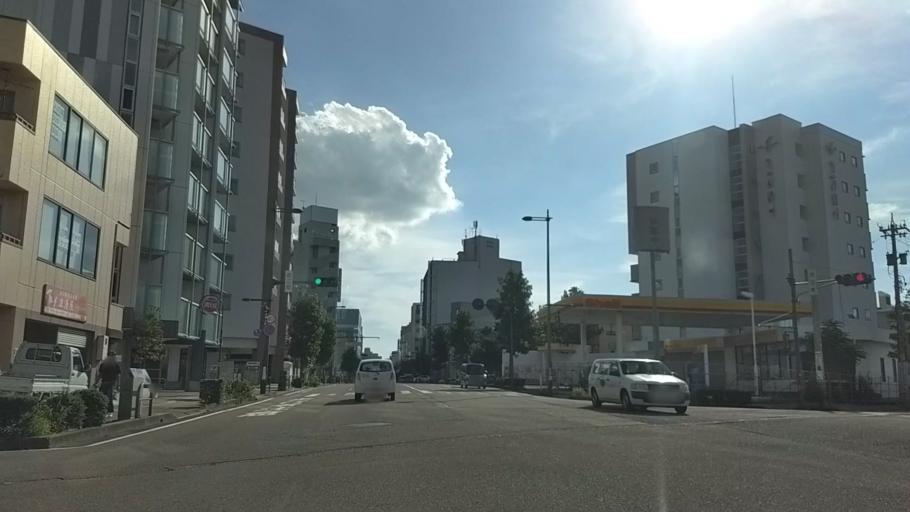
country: JP
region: Ishikawa
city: Kanazawa-shi
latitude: 36.5762
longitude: 136.6601
